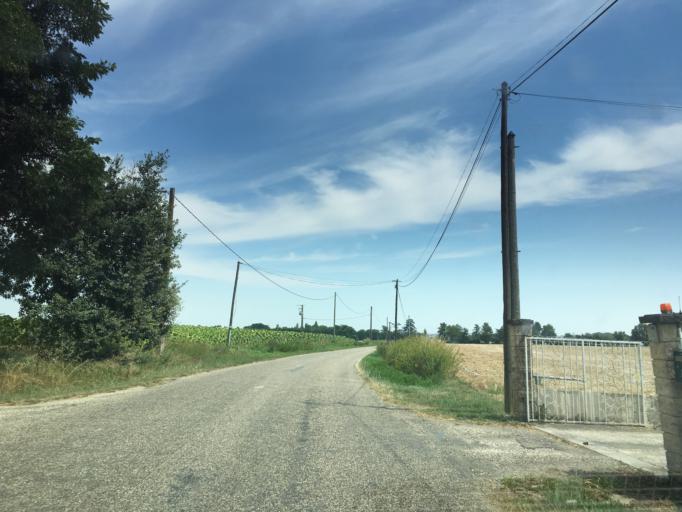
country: FR
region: Midi-Pyrenees
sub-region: Departement du Gers
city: Fleurance
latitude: 43.8160
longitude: 0.6199
